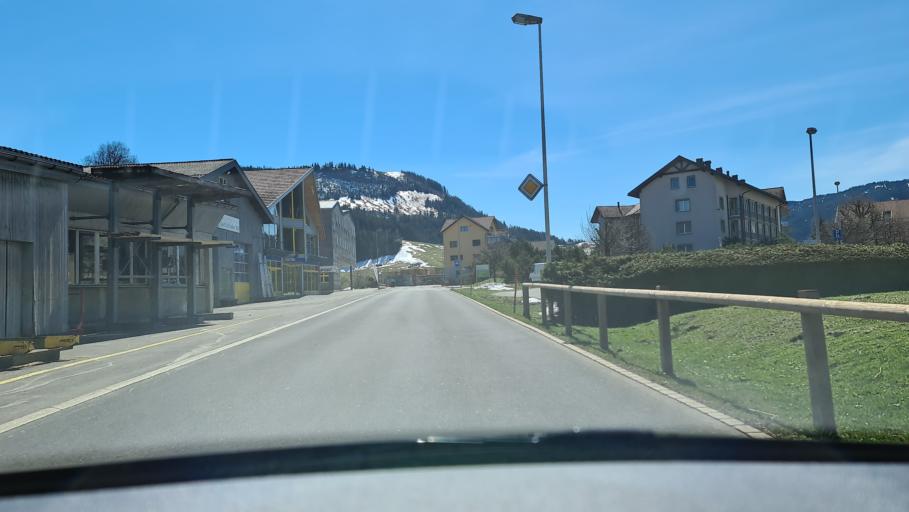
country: CH
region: Schwyz
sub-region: Bezirk Einsiedeln
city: Einsiedeln
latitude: 47.1226
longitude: 8.7427
